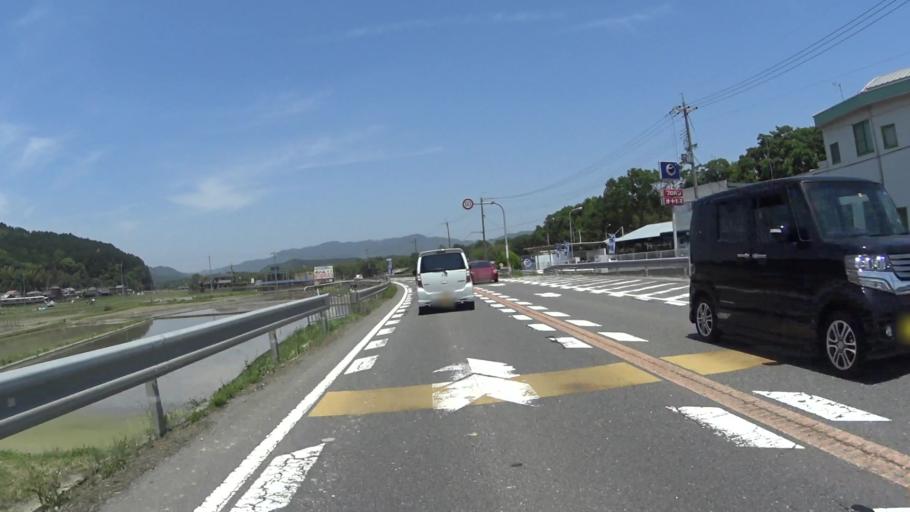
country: JP
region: Kyoto
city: Kameoka
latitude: 35.0560
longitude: 135.5480
